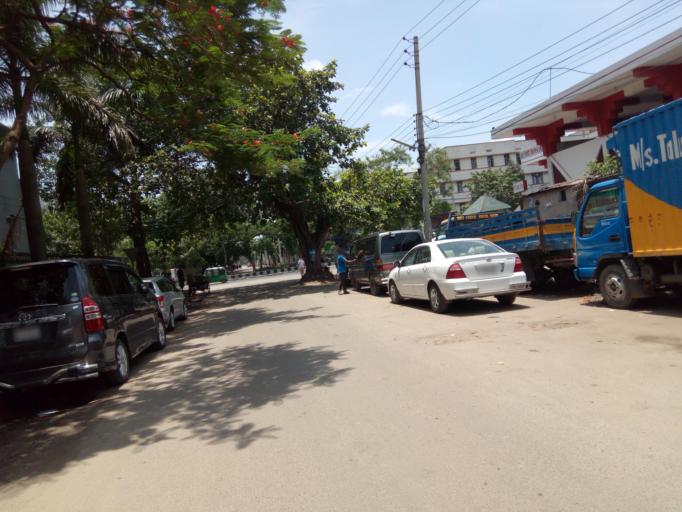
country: BD
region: Dhaka
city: Paltan
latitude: 23.7598
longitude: 90.3988
